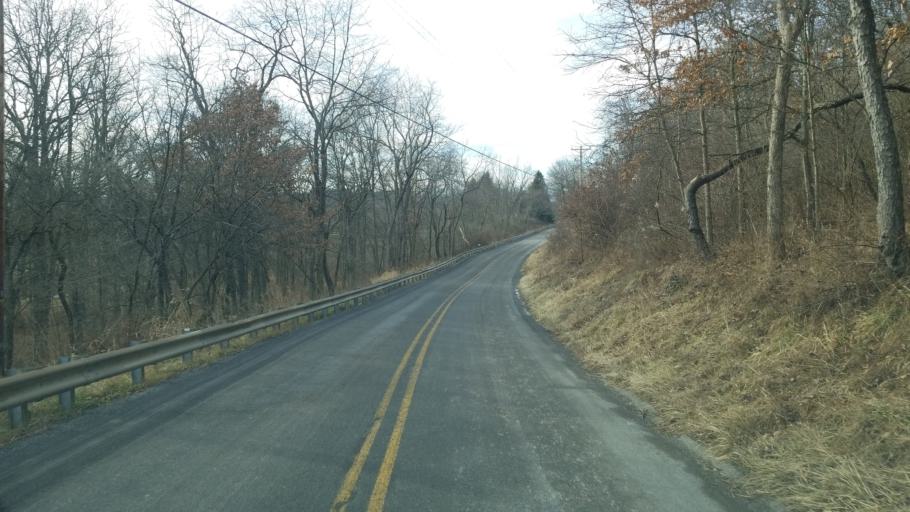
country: US
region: Pennsylvania
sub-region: Jefferson County
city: Punxsutawney
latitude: 40.8381
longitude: -79.1236
